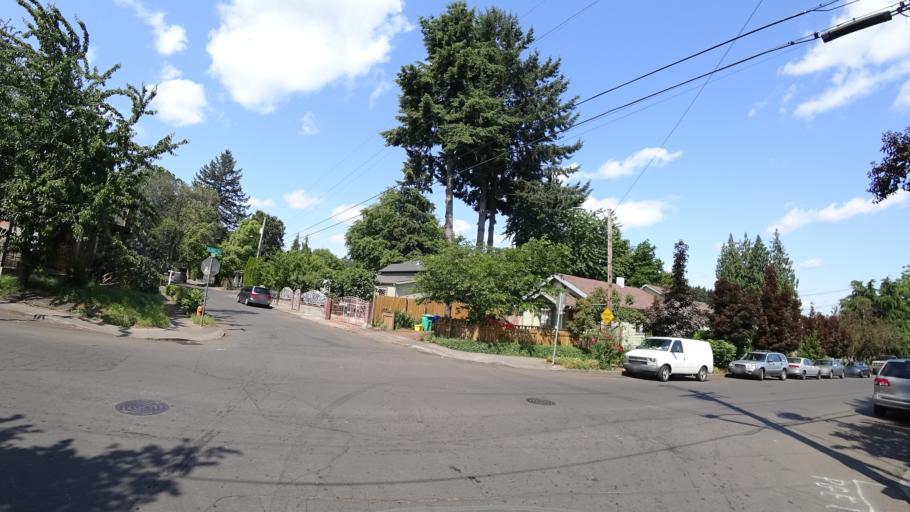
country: US
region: Oregon
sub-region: Washington County
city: West Haven
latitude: 45.5996
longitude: -122.7492
